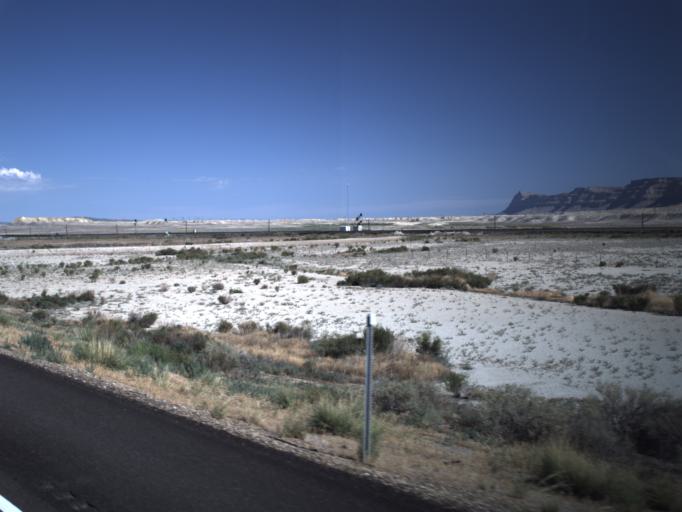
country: US
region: Utah
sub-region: Carbon County
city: East Carbon City
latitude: 39.0002
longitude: -110.2672
